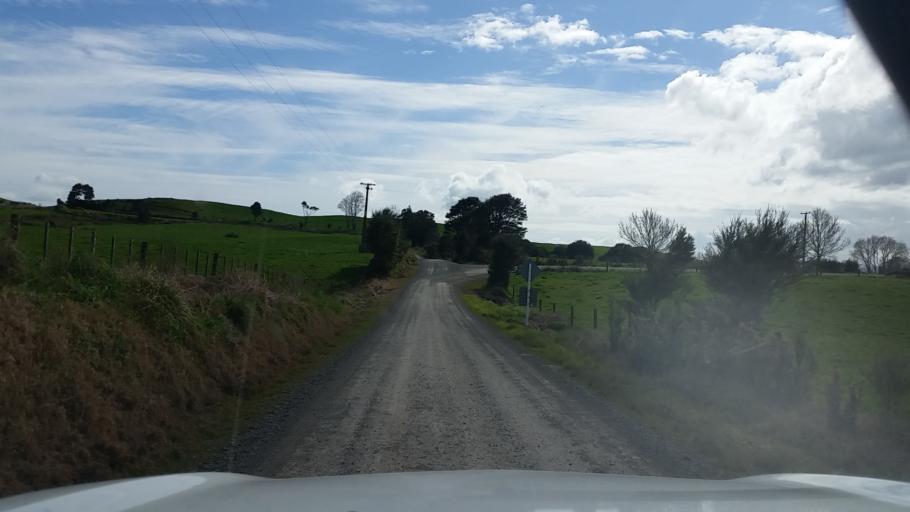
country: NZ
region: Waikato
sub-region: Hauraki District
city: Ngatea
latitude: -37.4500
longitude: 175.4988
